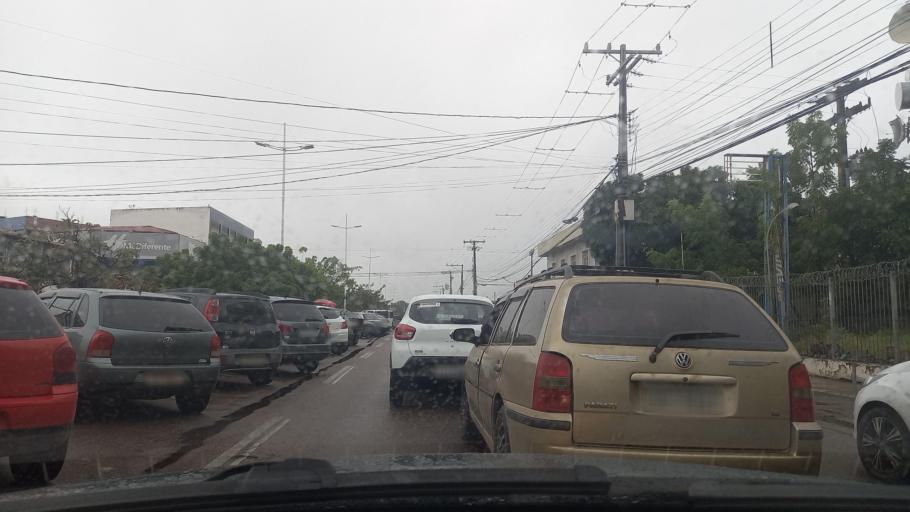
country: BR
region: Bahia
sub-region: Paulo Afonso
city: Paulo Afonso
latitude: -9.4023
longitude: -38.2291
